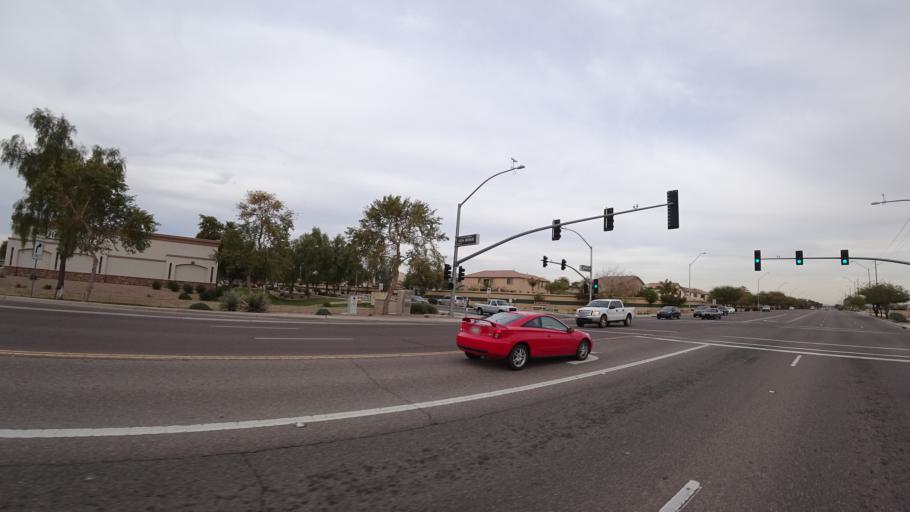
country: US
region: Arizona
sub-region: Maricopa County
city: Surprise
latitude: 33.6091
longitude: -112.3554
